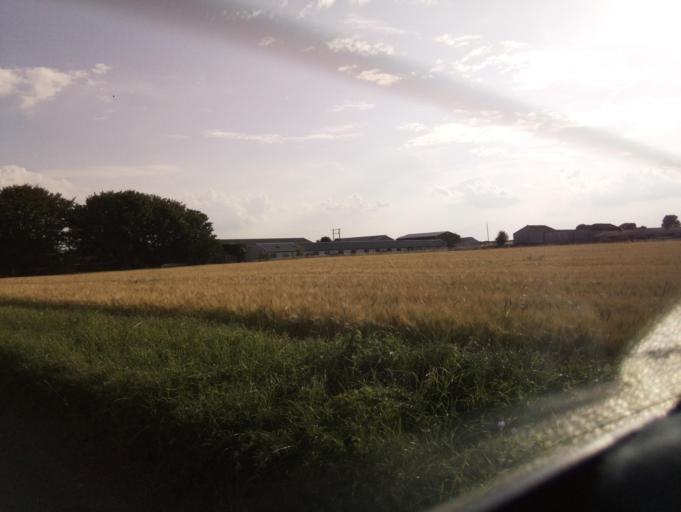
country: GB
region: England
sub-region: South Gloucestershire
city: Marshfield
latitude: 51.4717
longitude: -2.3118
